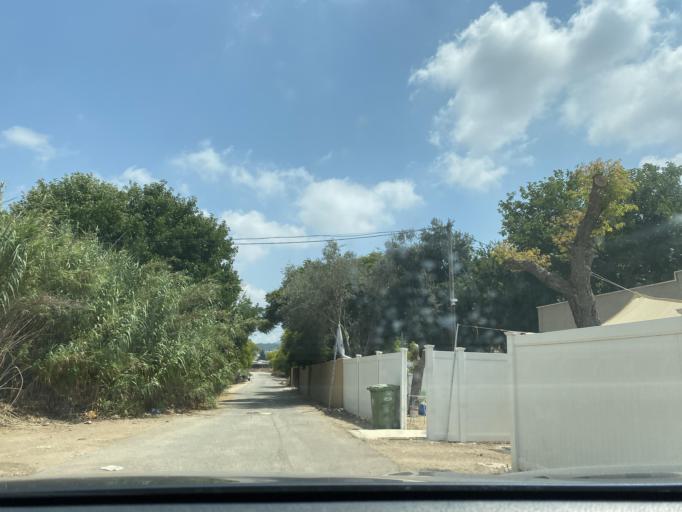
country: IL
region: Northern District
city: Kefar Weradim
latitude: 32.9987
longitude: 35.2982
